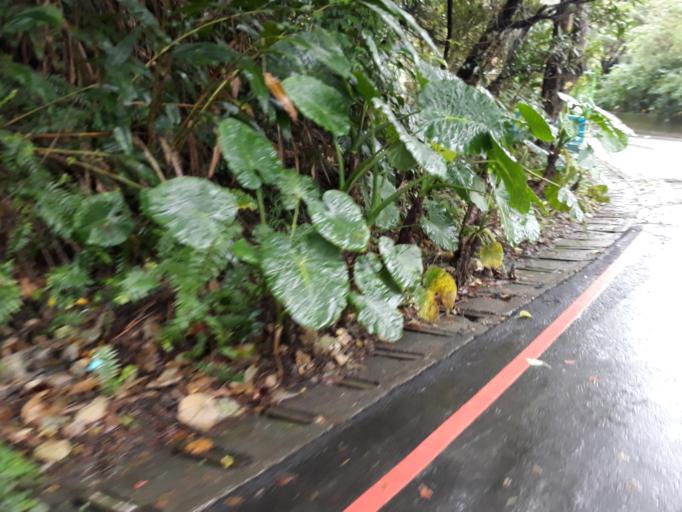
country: TW
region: Taipei
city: Taipei
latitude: 24.9943
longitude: 121.5892
